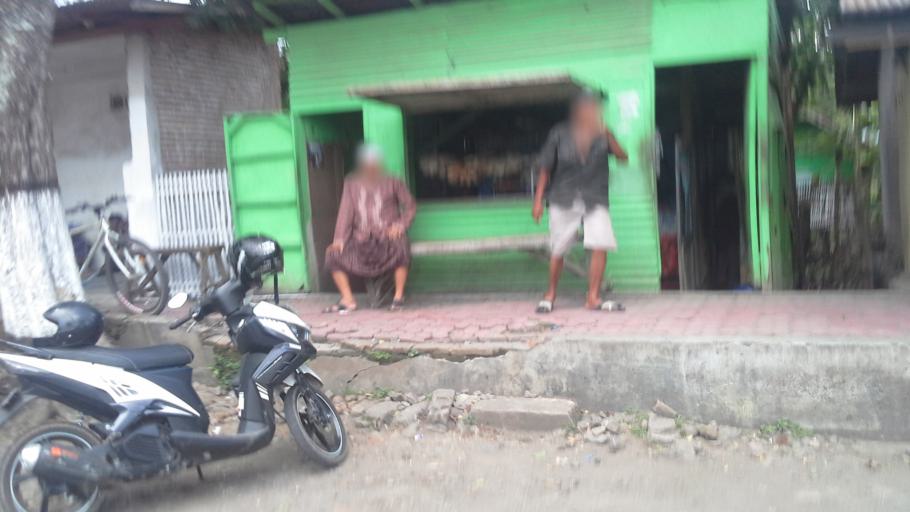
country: ID
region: East Java
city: Bondowoso
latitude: -7.9142
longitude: 113.8392
